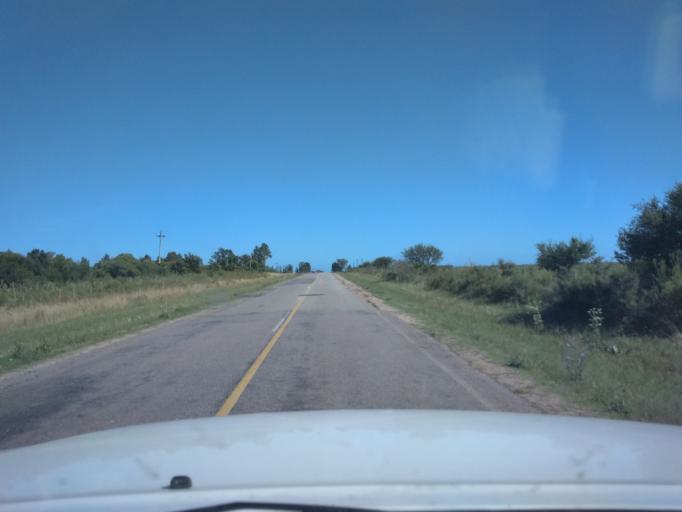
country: UY
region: Canelones
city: San Ramon
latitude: -34.2004
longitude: -55.9344
